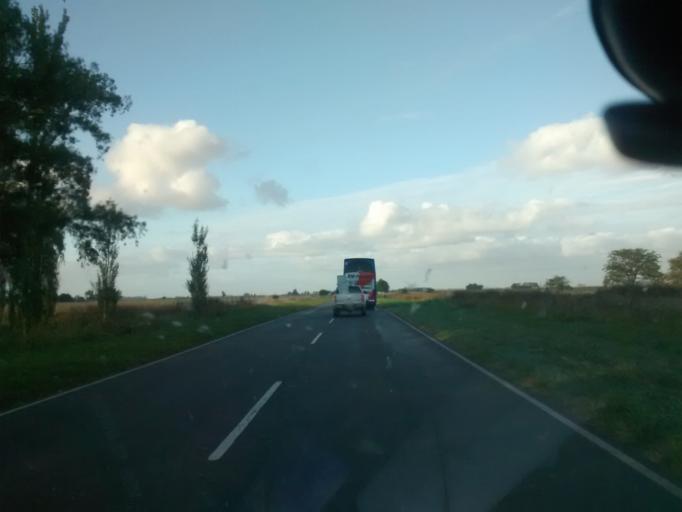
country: AR
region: Buenos Aires
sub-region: Partido de General Belgrano
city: General Belgrano
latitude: -35.8606
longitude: -58.6124
